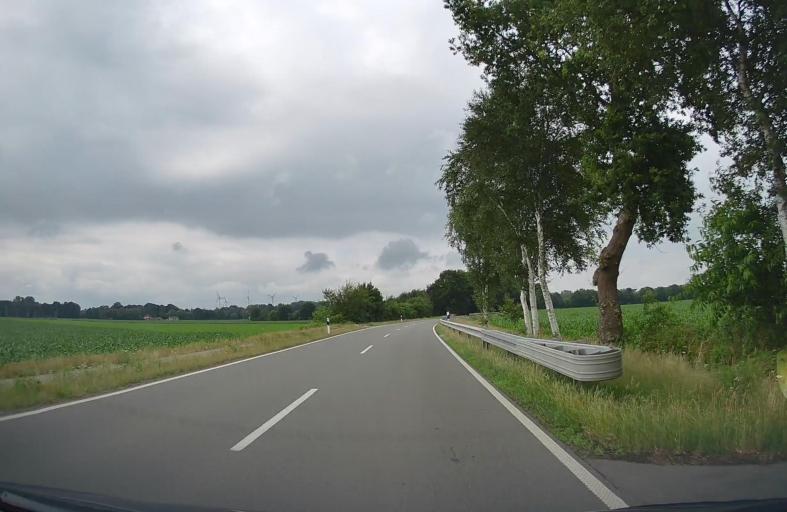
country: DE
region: Lower Saxony
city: Friesoythe
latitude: 53.0522
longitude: 7.8135
